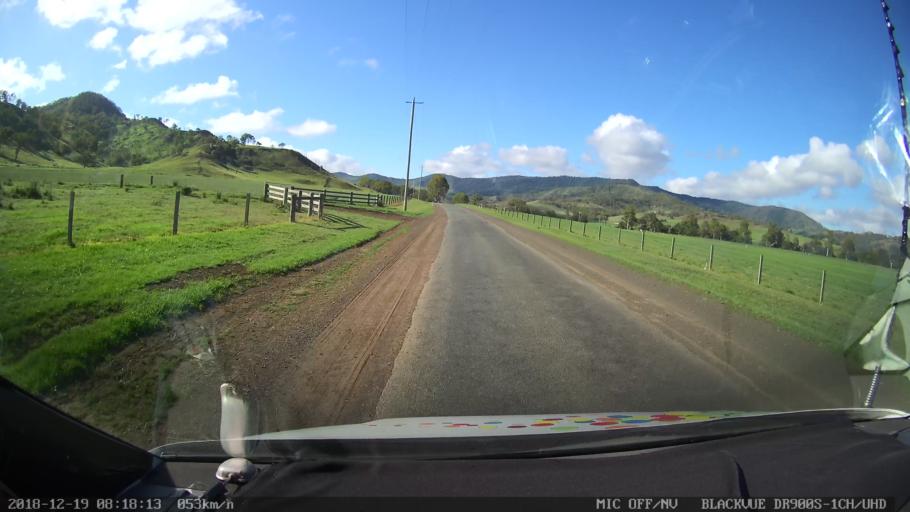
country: AU
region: New South Wales
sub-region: Kyogle
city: Kyogle
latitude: -28.2713
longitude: 152.9100
